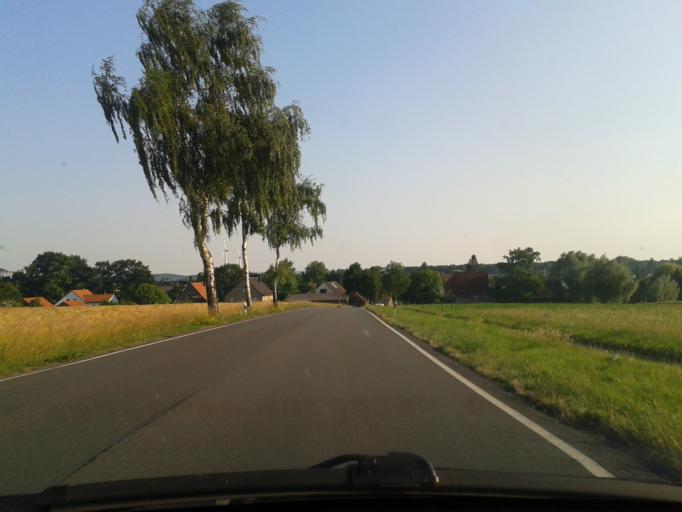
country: DE
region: North Rhine-Westphalia
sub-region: Regierungsbezirk Detmold
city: Lemgo
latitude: 51.9934
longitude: 8.9153
